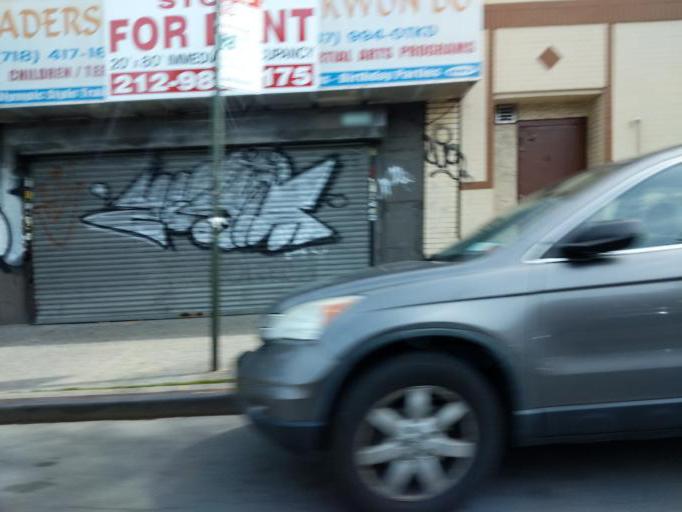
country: US
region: New York
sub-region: Kings County
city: East New York
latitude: 40.6995
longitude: -73.9052
